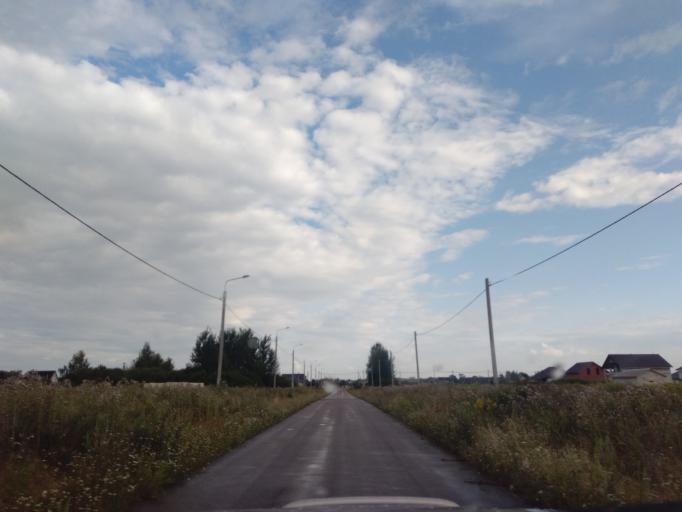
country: BY
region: Minsk
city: Kapyl'
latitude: 53.1655
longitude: 27.0784
